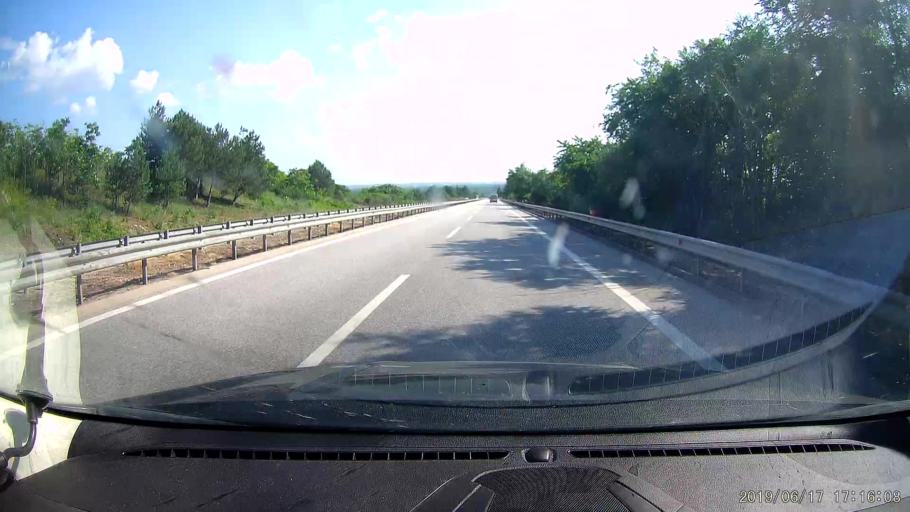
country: GR
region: East Macedonia and Thrace
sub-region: Nomos Evrou
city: Kastanies
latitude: 41.6958
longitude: 26.4850
